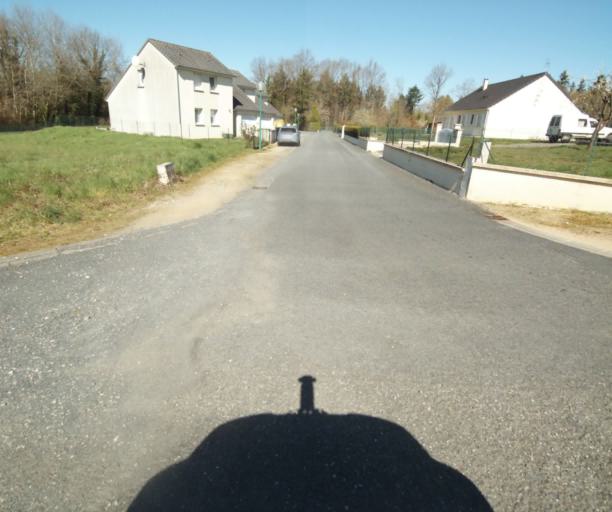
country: FR
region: Limousin
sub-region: Departement de la Correze
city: Chamboulive
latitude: 45.4266
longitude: 1.7030
